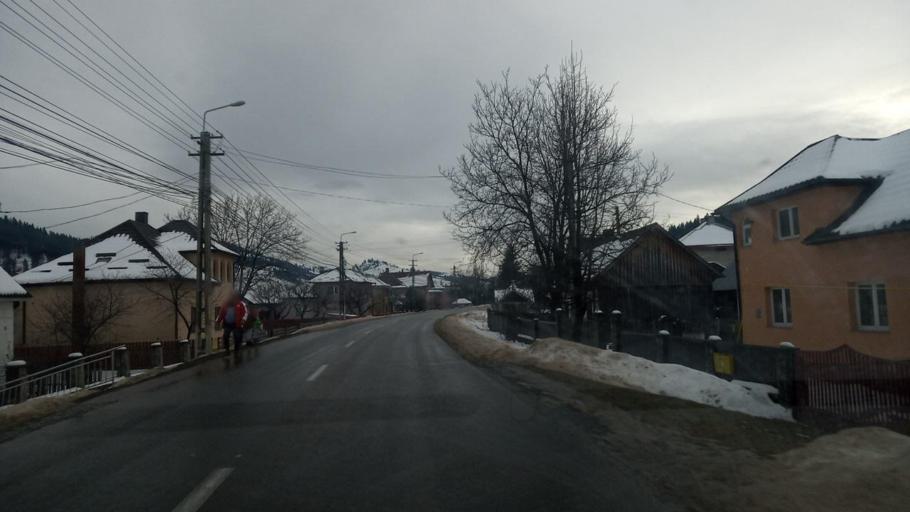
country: RO
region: Suceava
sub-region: Comuna Frasin
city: Frasin
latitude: 47.5258
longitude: 25.7981
